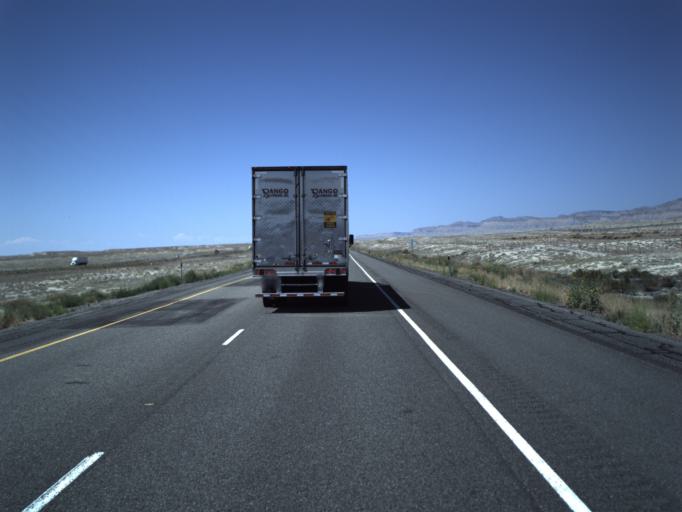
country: US
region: Utah
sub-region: Grand County
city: Moab
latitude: 38.9352
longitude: -109.4550
